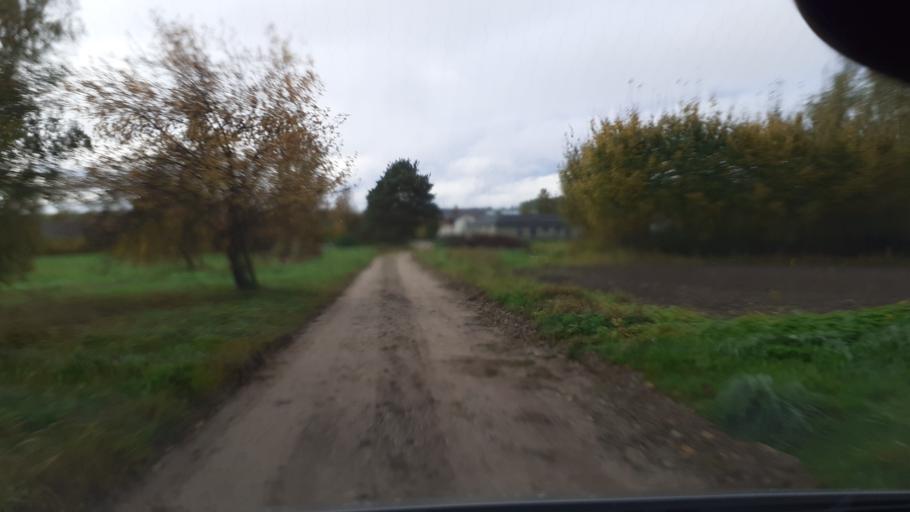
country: LV
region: Kuldigas Rajons
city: Kuldiga
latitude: 56.9723
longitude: 21.9392
